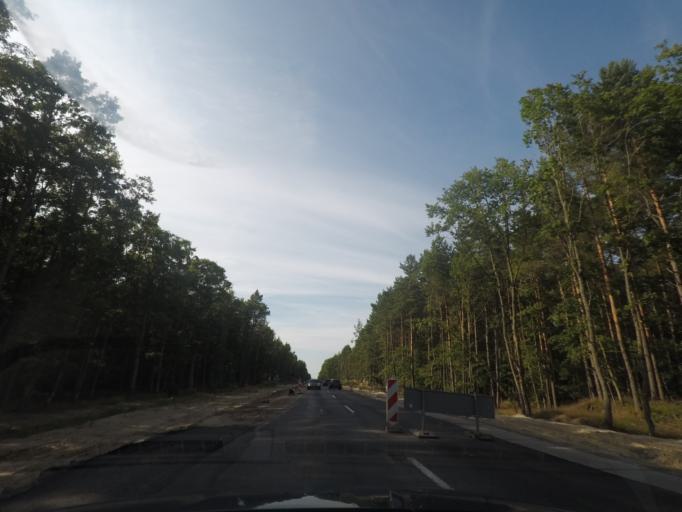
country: PL
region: Pomeranian Voivodeship
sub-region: Powiat leborski
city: Leba
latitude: 54.7028
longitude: 17.5856
